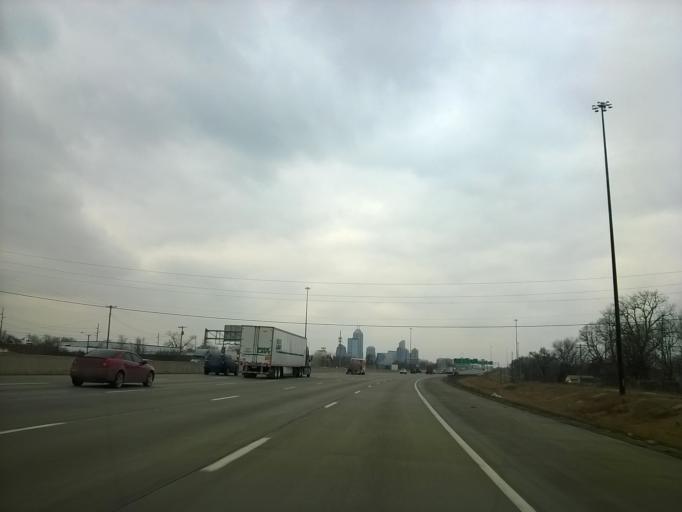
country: US
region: Indiana
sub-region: Marion County
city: Indianapolis
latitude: 39.7901
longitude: -86.1280
